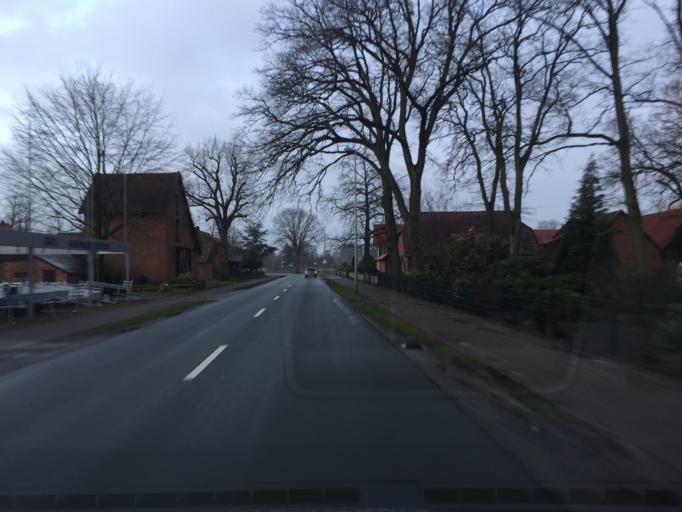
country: DE
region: Lower Saxony
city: Pennigsehl
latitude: 52.6418
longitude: 9.0264
